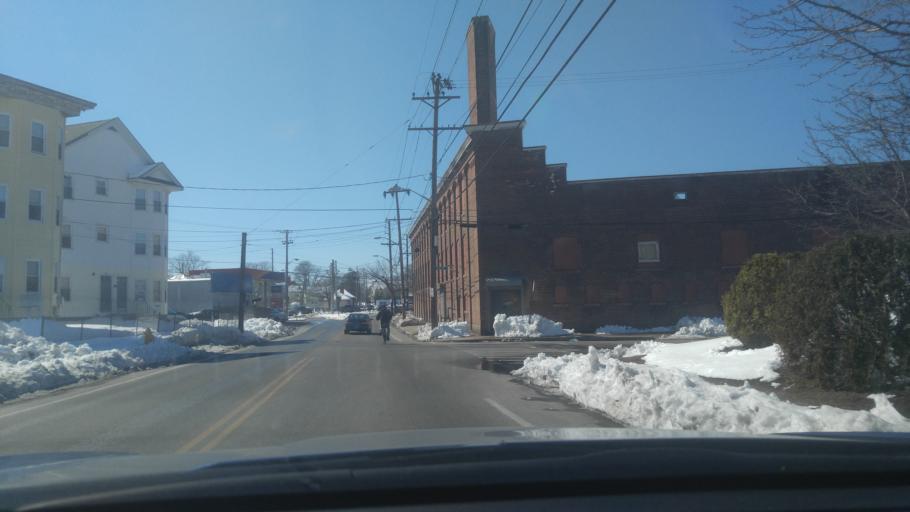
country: US
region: Rhode Island
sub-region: Providence County
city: Pawtucket
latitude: 41.8857
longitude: -71.3688
